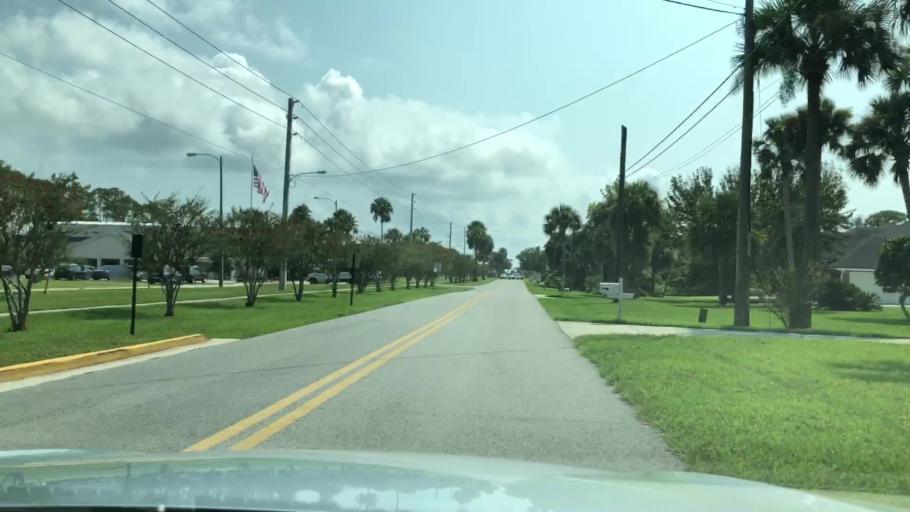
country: US
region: Florida
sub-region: Duval County
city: Neptune Beach
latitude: 30.3142
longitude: -81.4028
